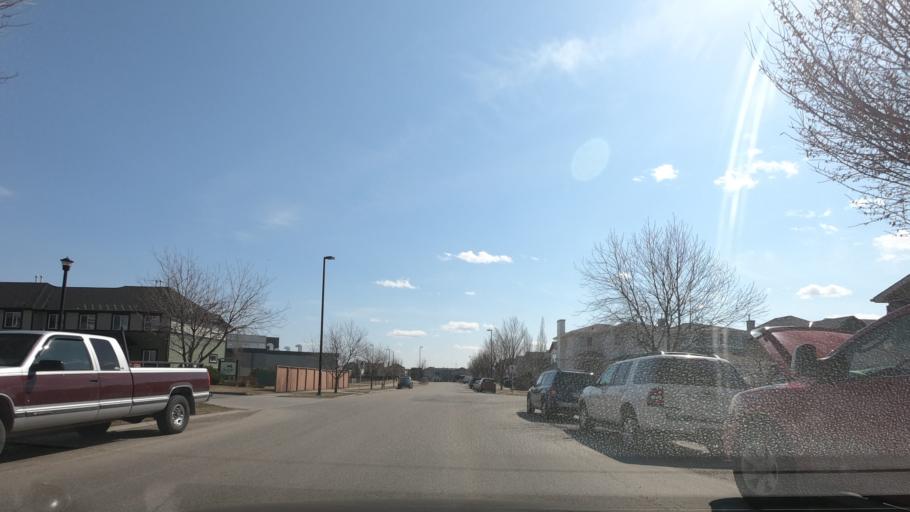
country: CA
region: Alberta
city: Airdrie
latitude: 51.2908
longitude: -114.0425
